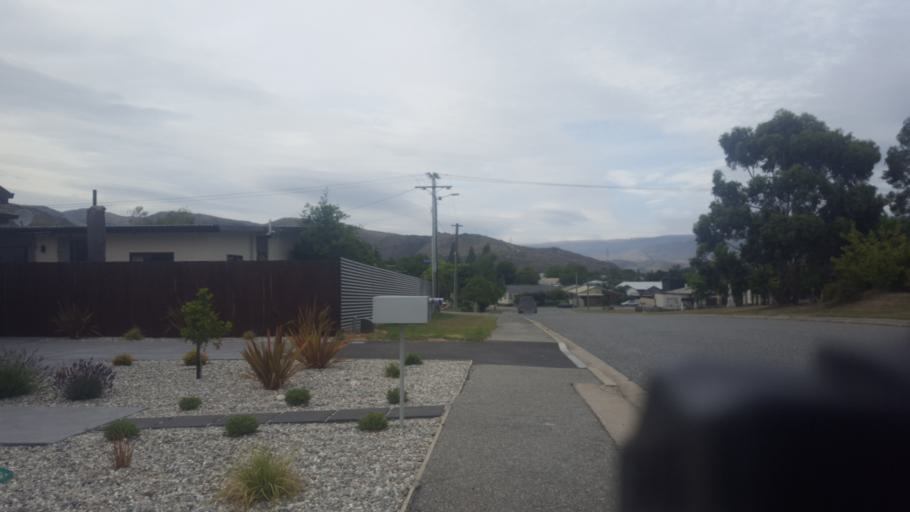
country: NZ
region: Otago
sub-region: Queenstown-Lakes District
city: Wanaka
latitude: -45.0423
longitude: 169.2107
